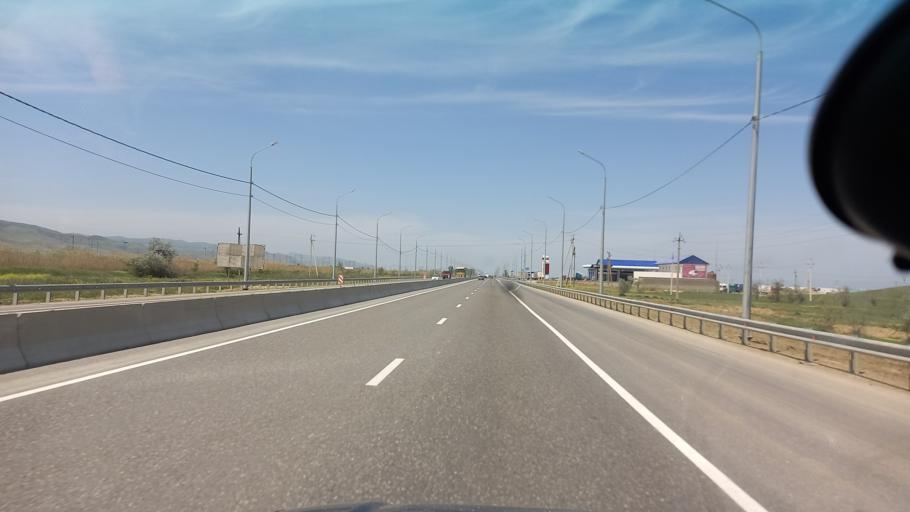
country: RU
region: Dagestan
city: Manas
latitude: 42.7402
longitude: 47.6600
